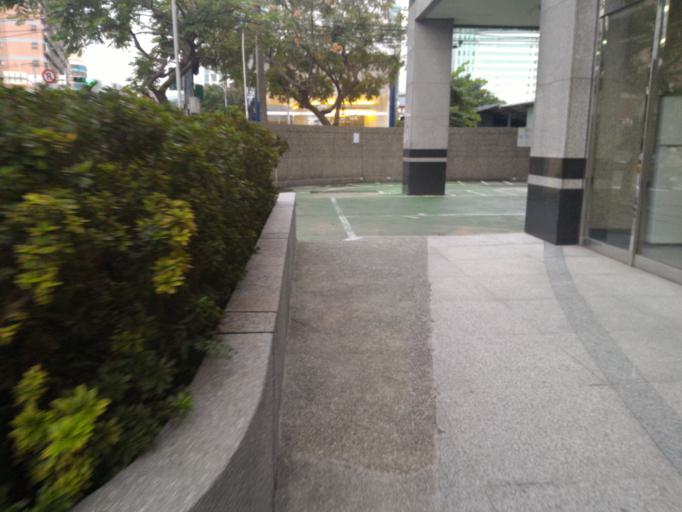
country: TW
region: Taipei
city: Taipei
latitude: 24.9869
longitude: 121.5371
